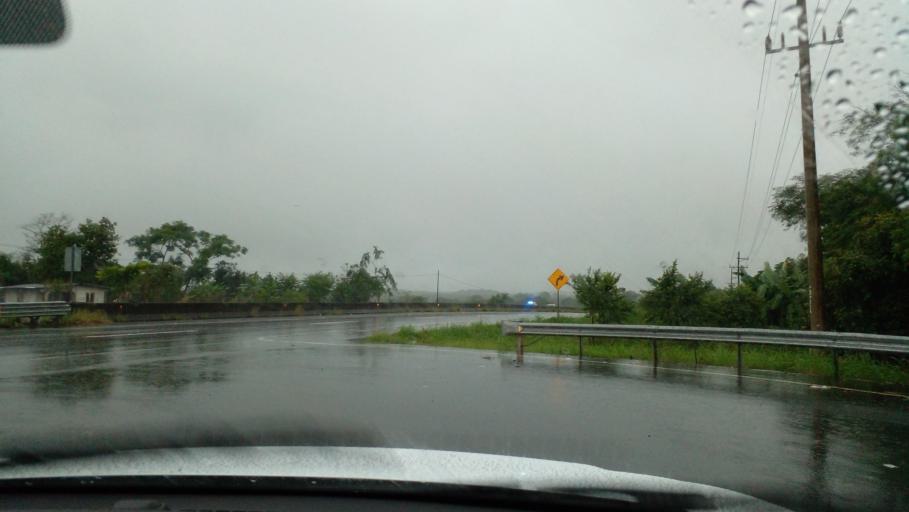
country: PA
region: Chiriqui
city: San Felix
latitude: 8.2831
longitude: -81.9526
